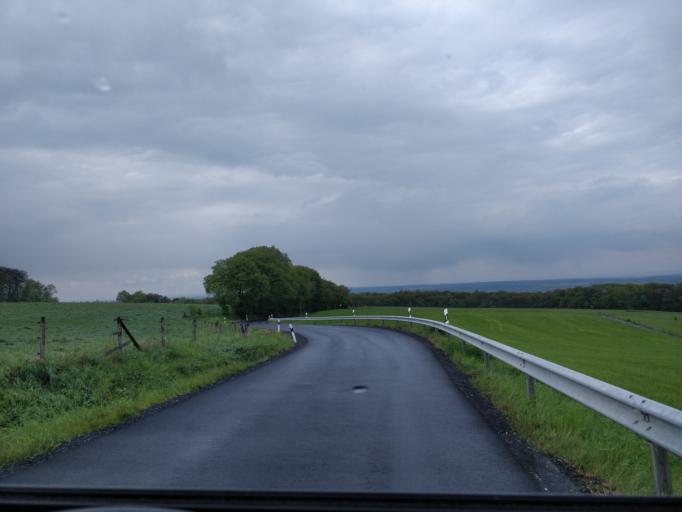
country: DE
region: Rheinland-Pfalz
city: Berg
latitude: 50.5821
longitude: 6.9453
